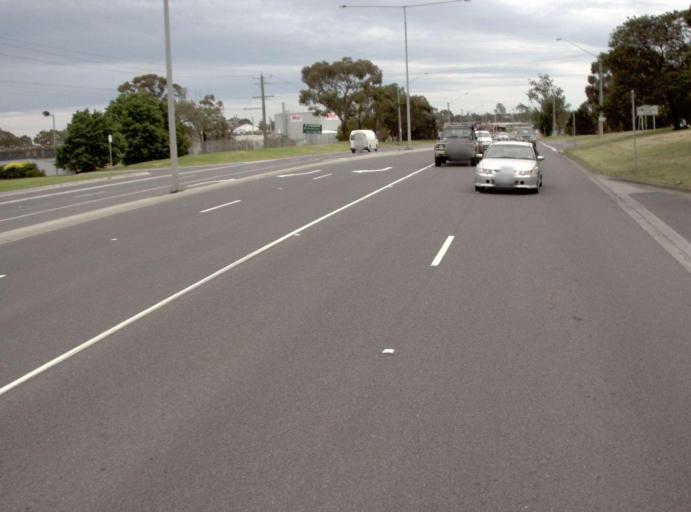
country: AU
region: Victoria
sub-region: Casey
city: Doveton
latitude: -38.0051
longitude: 145.2276
